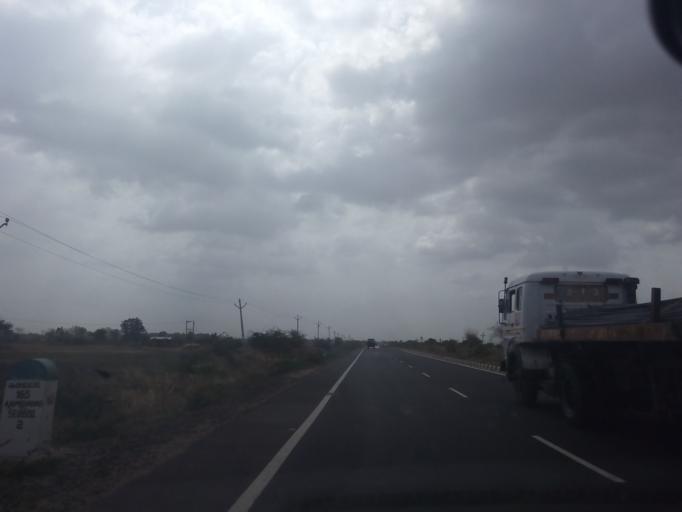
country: IN
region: Gujarat
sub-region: Surendranagar
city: Halvad
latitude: 23.0061
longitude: 71.0737
